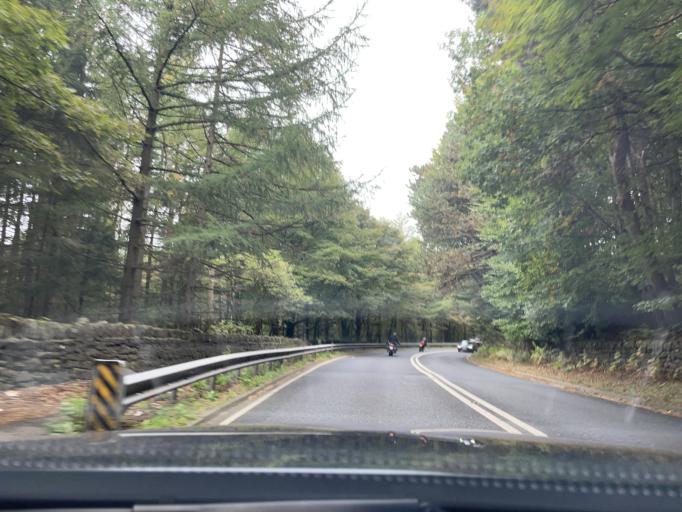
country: GB
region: England
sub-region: Sheffield
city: Bradfield
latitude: 53.3808
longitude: -1.5968
